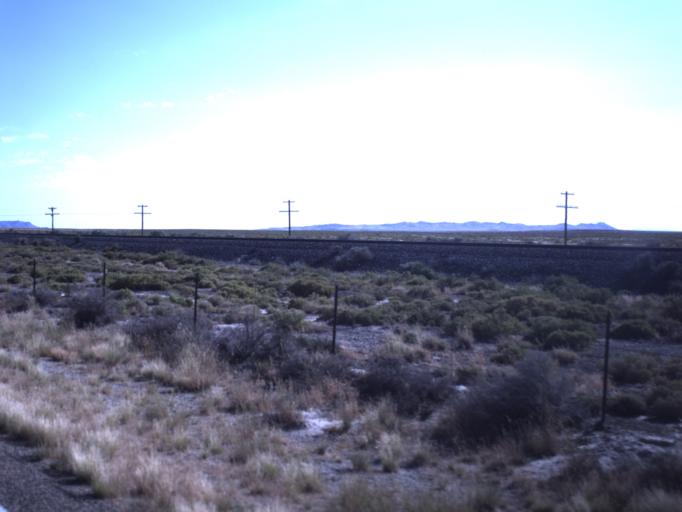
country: US
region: Utah
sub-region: Beaver County
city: Milford
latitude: 38.6352
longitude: -112.9838
